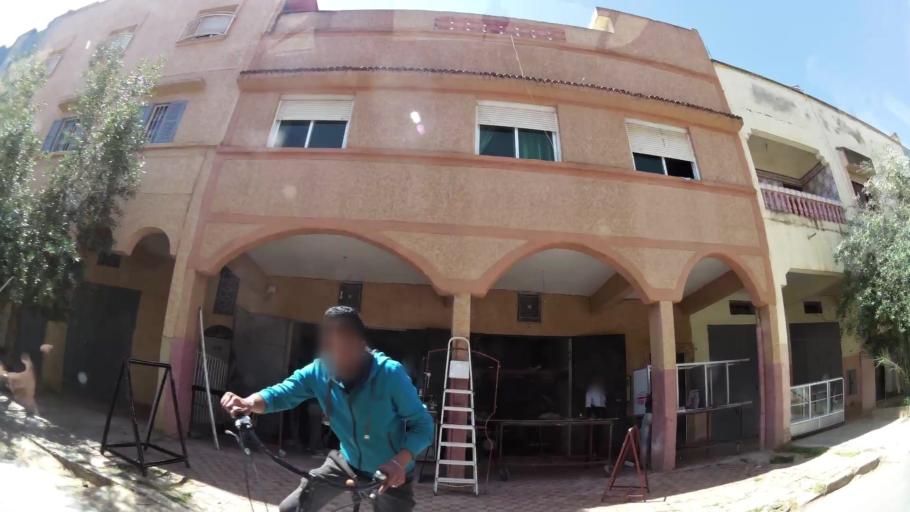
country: MA
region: Rabat-Sale-Zemmour-Zaer
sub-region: Khemisset
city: Khemisset
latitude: 33.8105
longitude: -6.0702
